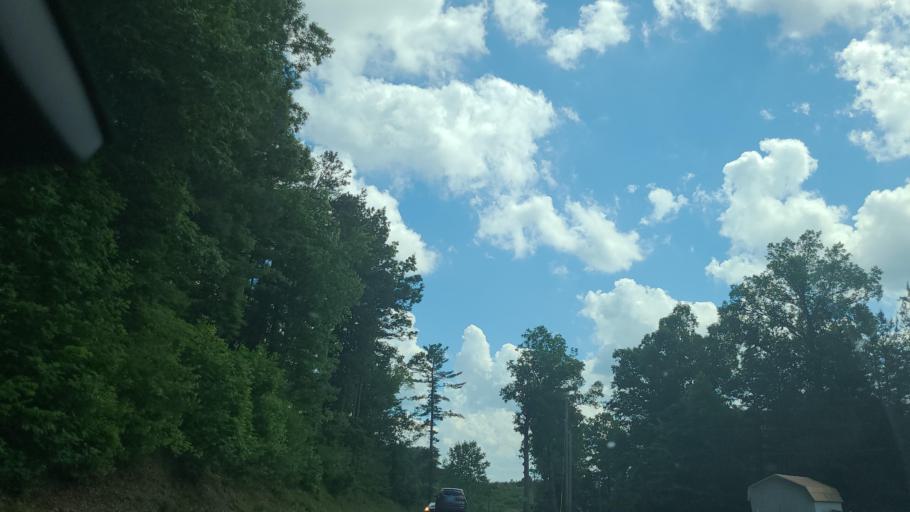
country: US
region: Kentucky
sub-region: Whitley County
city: Corbin
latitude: 36.8970
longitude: -84.1819
